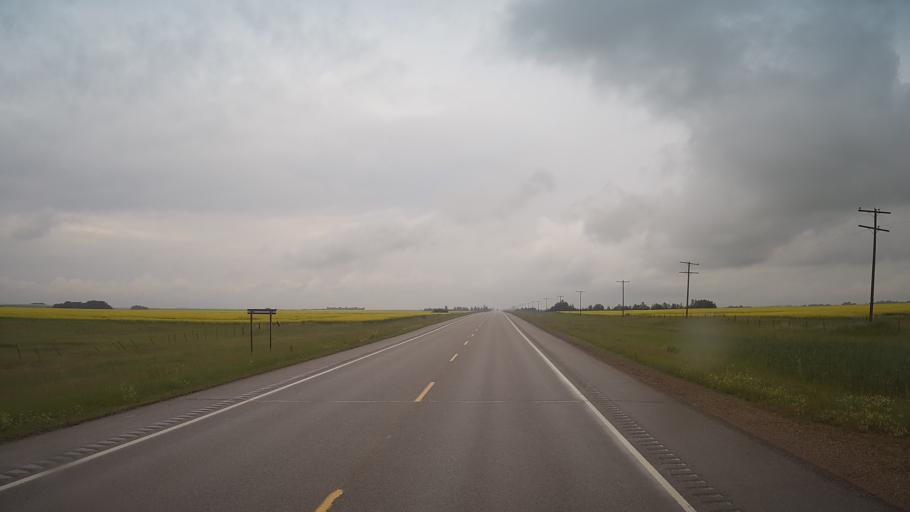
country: CA
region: Saskatchewan
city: Unity
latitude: 52.4349
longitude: -109.0043
